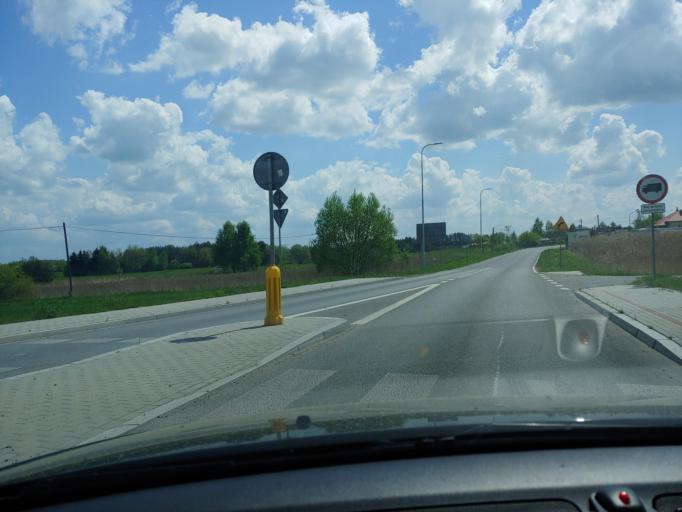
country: PL
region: Subcarpathian Voivodeship
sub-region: Powiat mielecki
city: Radomysl Wielki
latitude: 50.2070
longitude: 21.2797
